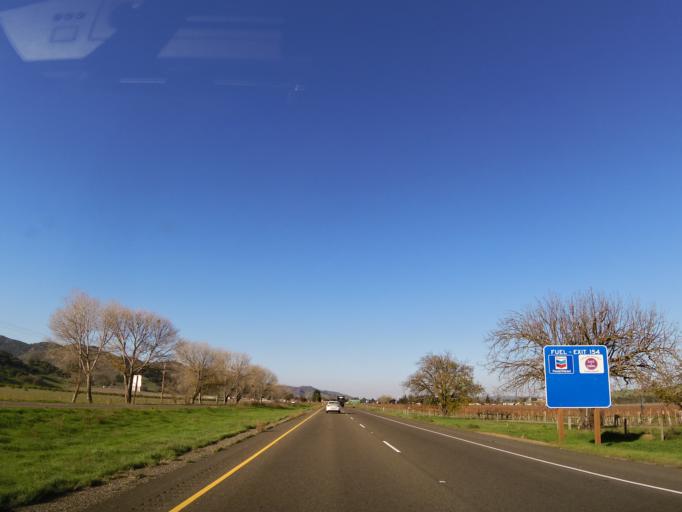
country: US
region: California
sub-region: Santa Barbara County
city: Los Alamos
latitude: 34.7370
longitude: -120.2574
